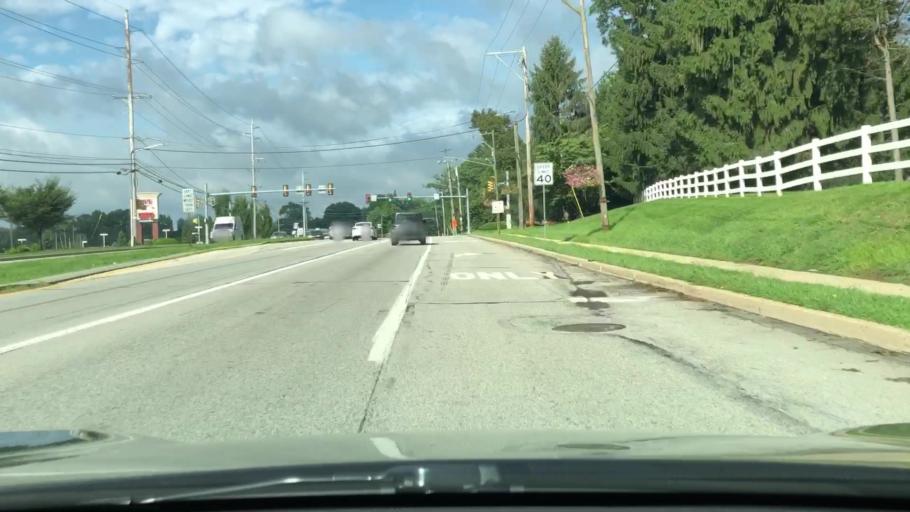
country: US
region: Pennsylvania
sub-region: Delaware County
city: Broomall
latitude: 39.9859
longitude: -75.4136
